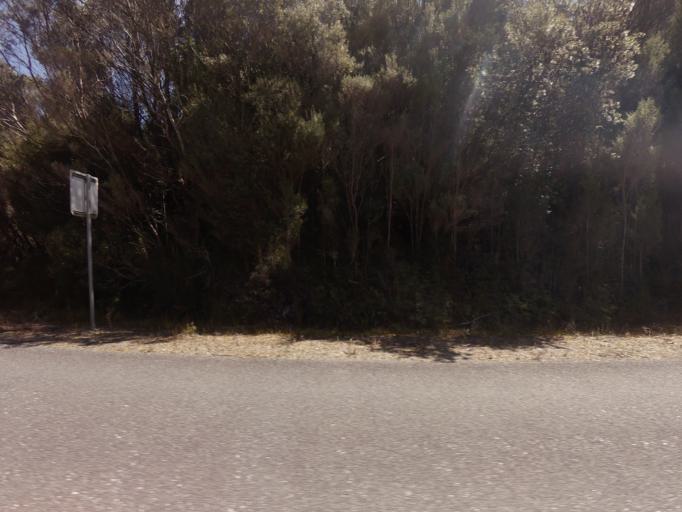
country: AU
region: Tasmania
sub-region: West Coast
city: Queenstown
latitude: -42.7713
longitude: 146.0431
